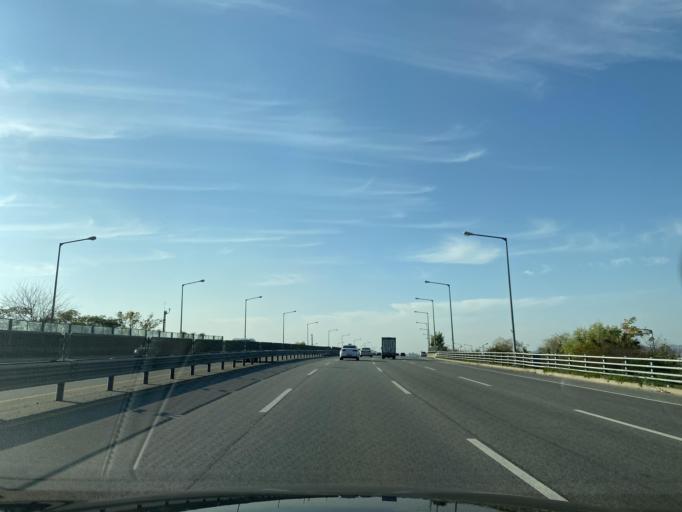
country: KR
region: Chungcheongnam-do
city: Asan
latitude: 36.7769
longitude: 127.0766
